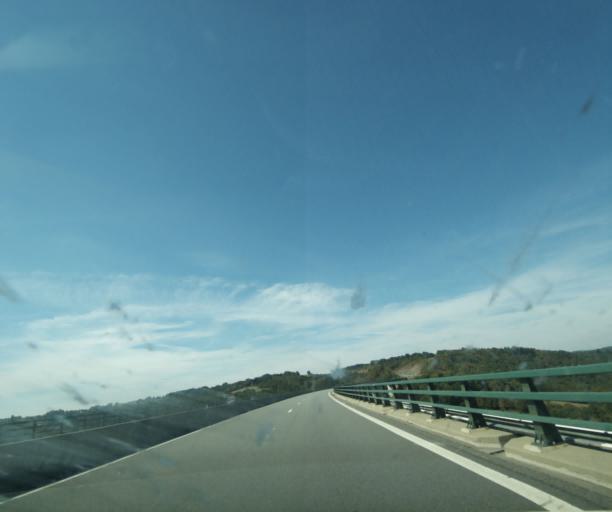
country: FR
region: Limousin
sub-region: Departement de la Correze
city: Naves
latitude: 45.3150
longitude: 1.7919
